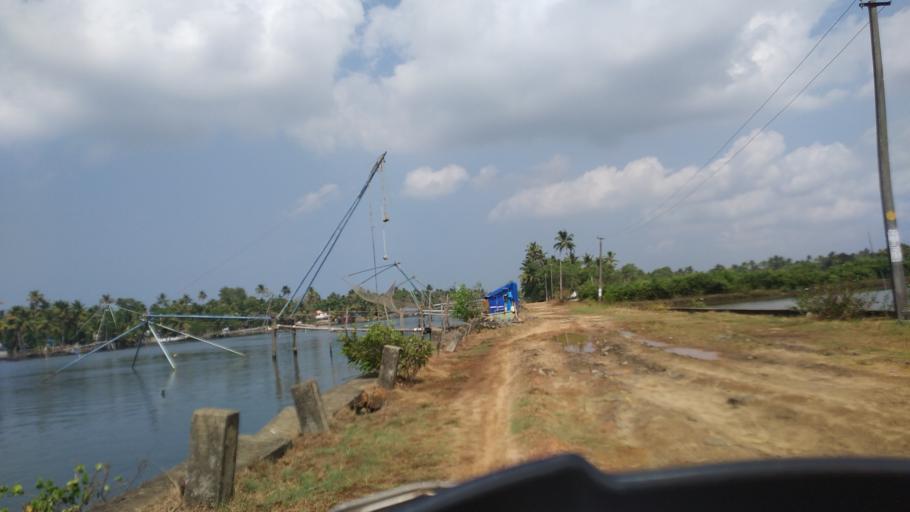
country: IN
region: Kerala
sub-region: Thrissur District
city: Kodungallur
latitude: 10.1369
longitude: 76.2055
